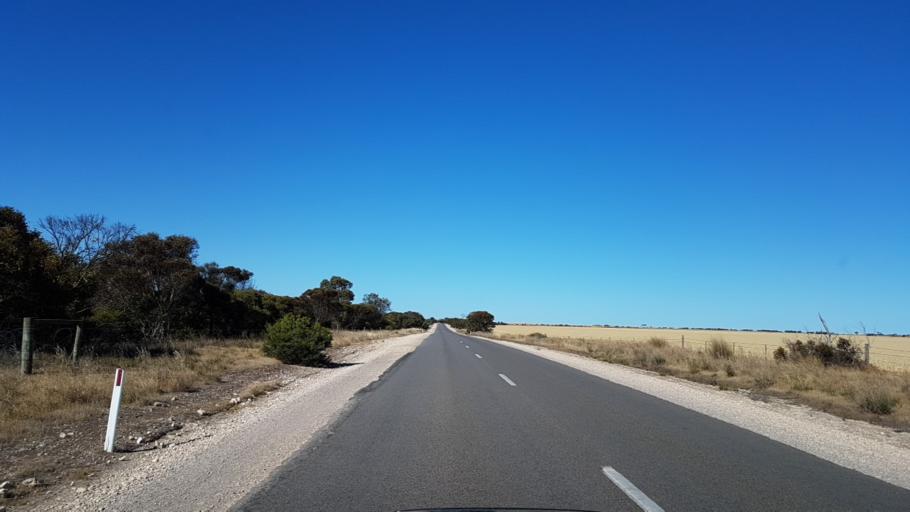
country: AU
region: South Australia
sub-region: Yorke Peninsula
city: Honiton
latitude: -34.8282
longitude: 137.5444
